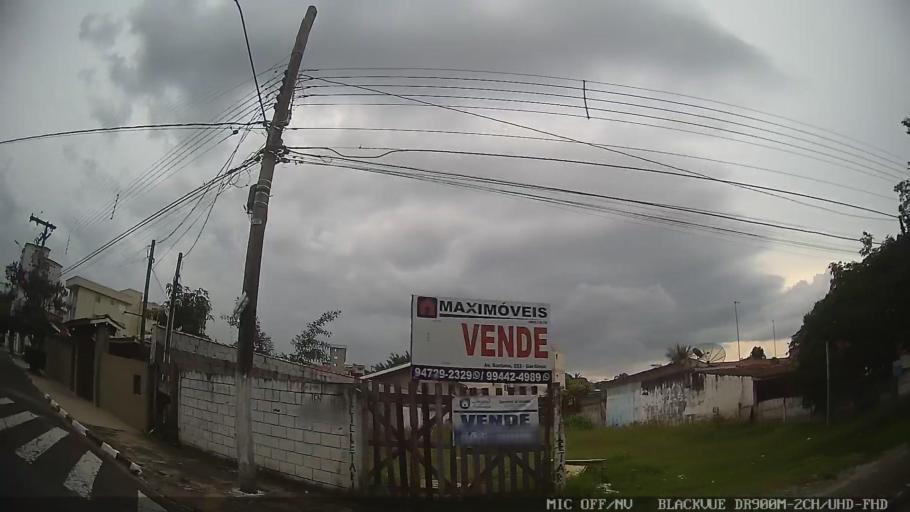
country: BR
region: Sao Paulo
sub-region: Atibaia
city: Atibaia
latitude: -23.1284
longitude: -46.5556
